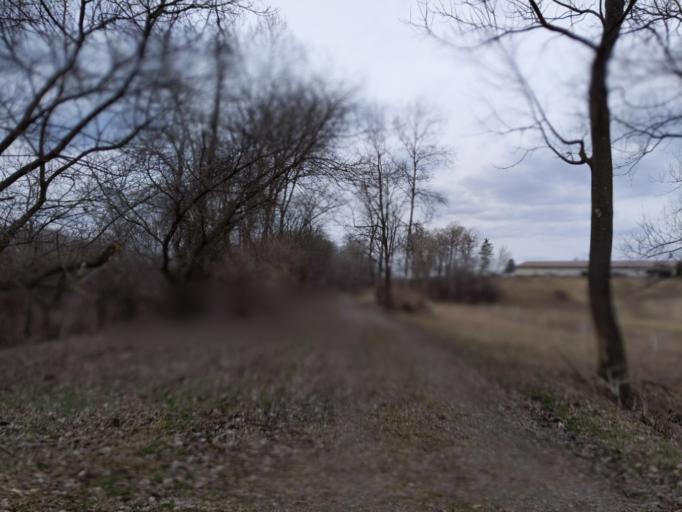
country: US
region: New York
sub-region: Tompkins County
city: Dryden
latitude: 42.5027
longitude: -76.3383
